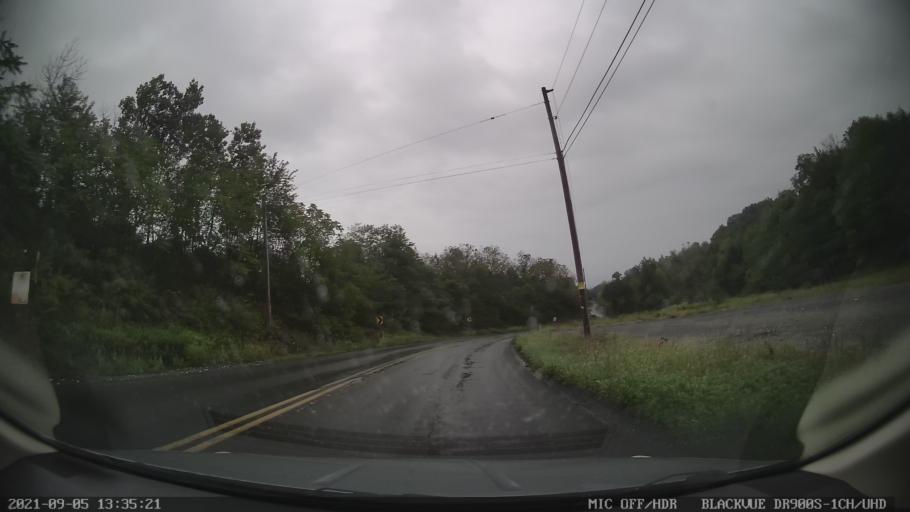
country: US
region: Pennsylvania
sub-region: Lehigh County
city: Breinigsville
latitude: 40.5775
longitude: -75.6732
